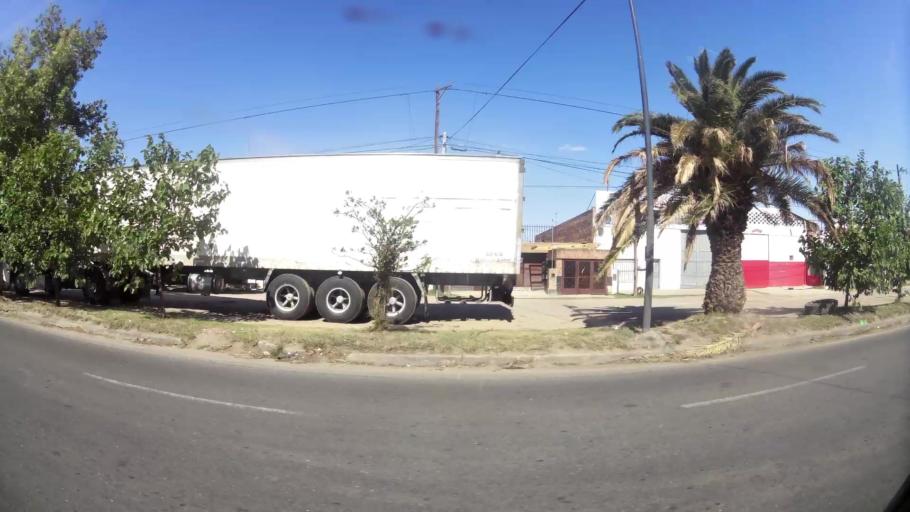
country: AR
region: Cordoba
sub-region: Departamento de Capital
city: Cordoba
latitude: -31.3660
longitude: -64.1761
